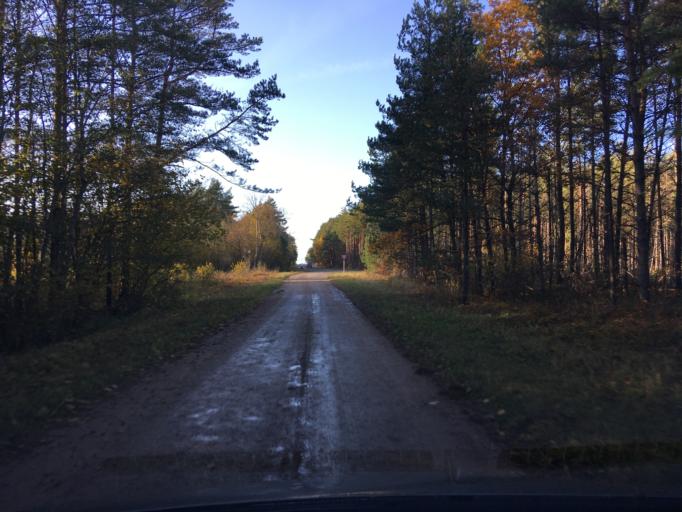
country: EE
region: Laeaene
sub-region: Lihula vald
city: Lihula
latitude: 58.5693
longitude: 23.7516
